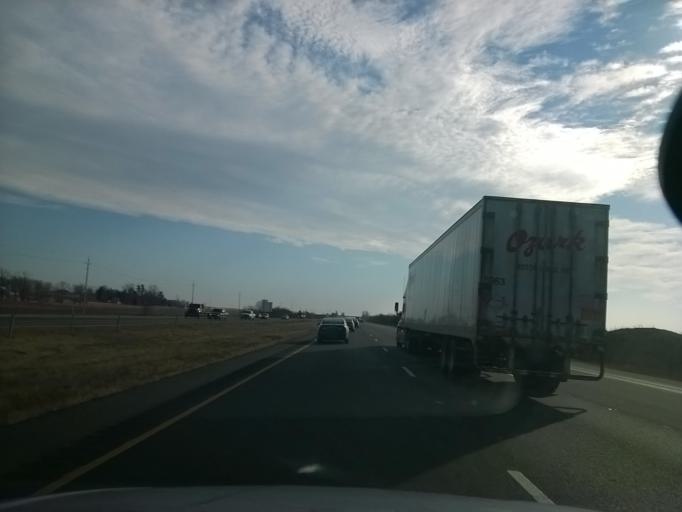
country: US
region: Indiana
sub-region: Johnson County
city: Edinburgh
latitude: 39.3584
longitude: -85.9425
